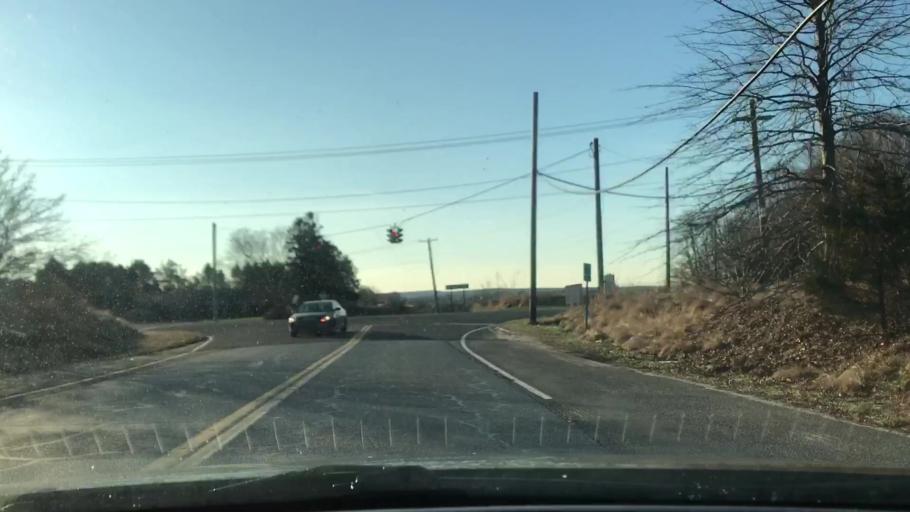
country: US
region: New York
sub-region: Suffolk County
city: Calverton
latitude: 40.9264
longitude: -72.7362
